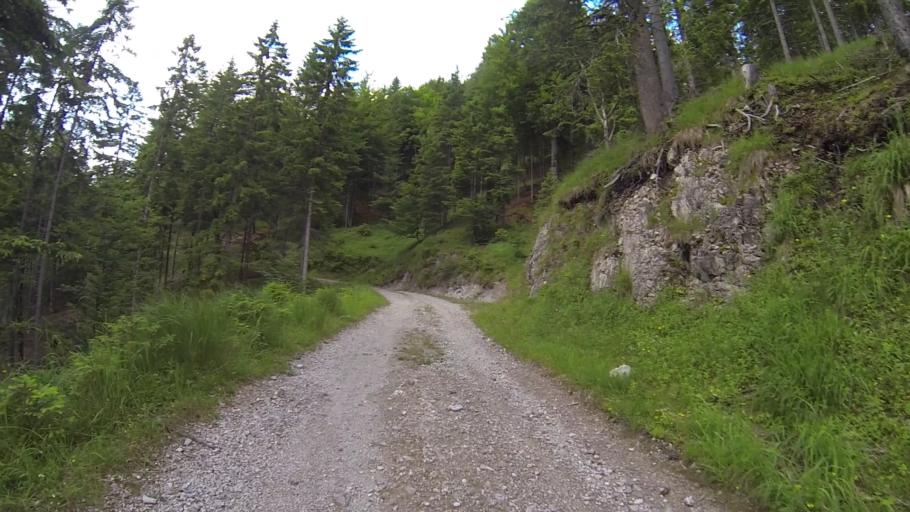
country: AT
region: Tyrol
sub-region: Politischer Bezirk Reutte
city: Breitenwang
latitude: 47.5037
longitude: 10.7626
